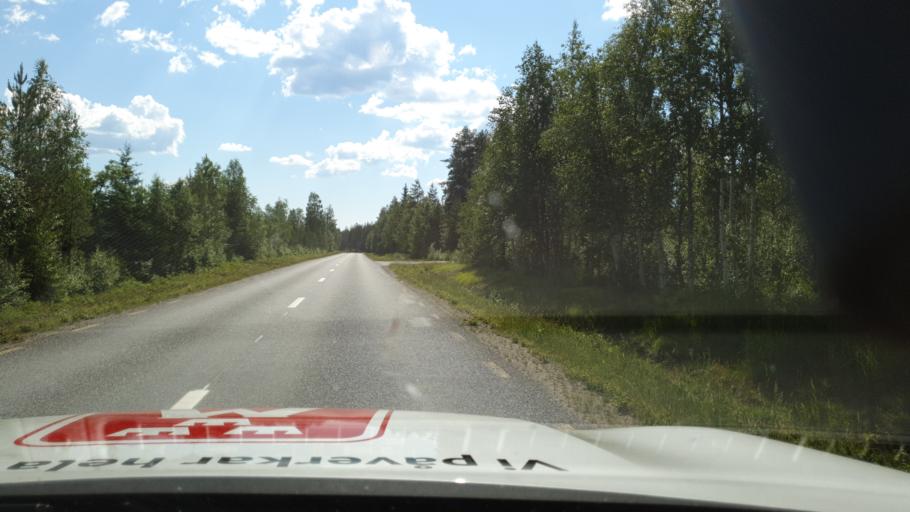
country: SE
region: Vaesterbotten
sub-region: Skelleftea Kommun
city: Burtraesk
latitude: 64.4903
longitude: 20.4352
